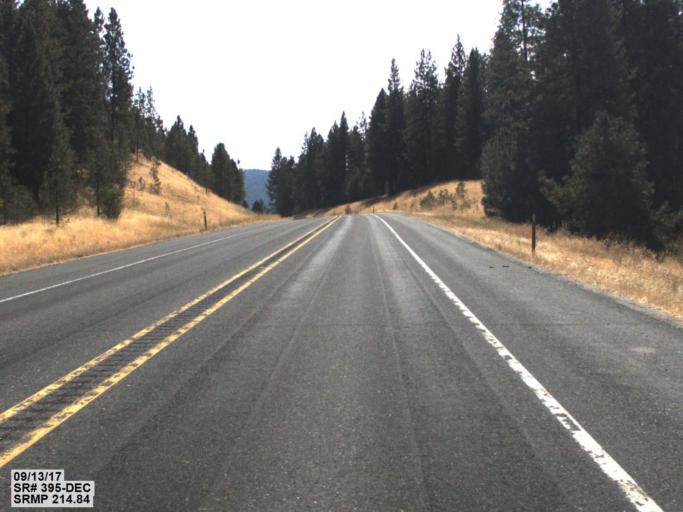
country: US
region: Washington
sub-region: Stevens County
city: Chewelah
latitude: 48.3431
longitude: -117.8325
